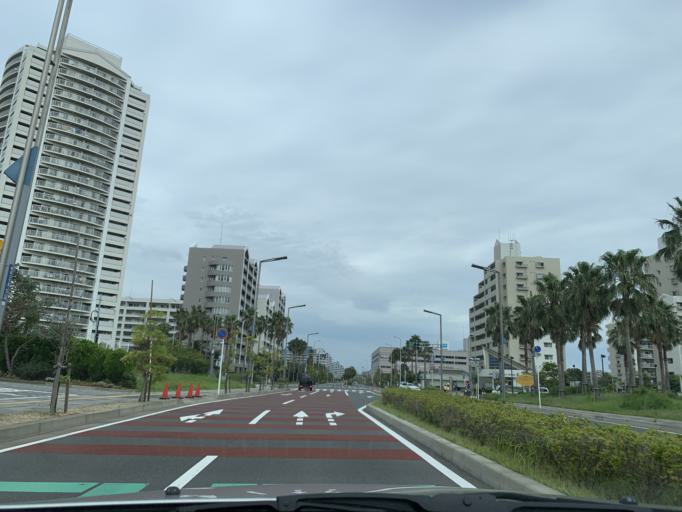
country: JP
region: Tokyo
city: Urayasu
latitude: 35.6408
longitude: 139.9189
